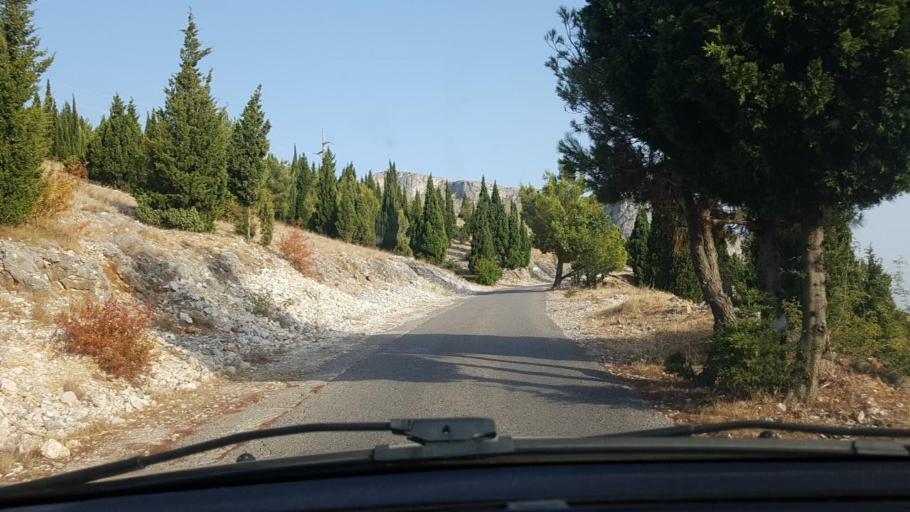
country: BA
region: Federation of Bosnia and Herzegovina
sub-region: Hercegovacko-Bosanski Kanton
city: Mostar
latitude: 43.3515
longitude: 17.8215
